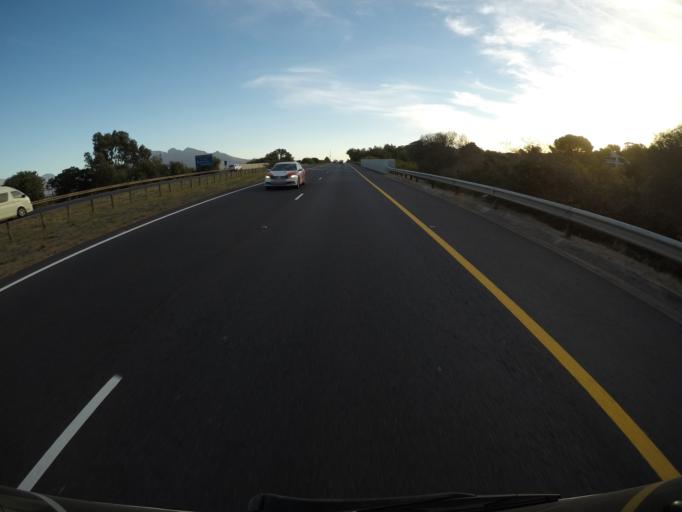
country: ZA
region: Western Cape
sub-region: Cape Winelands District Municipality
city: Paarl
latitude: -33.7750
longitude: 18.9583
